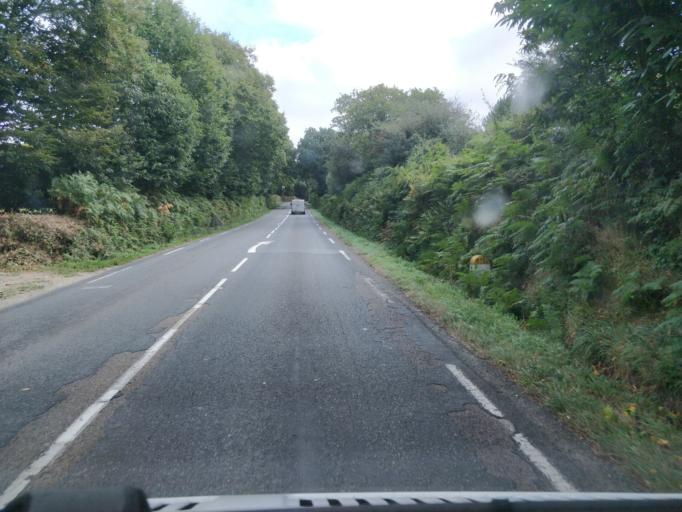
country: FR
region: Brittany
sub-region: Departement du Finistere
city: Pluguffan
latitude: 48.0013
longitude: -4.1819
